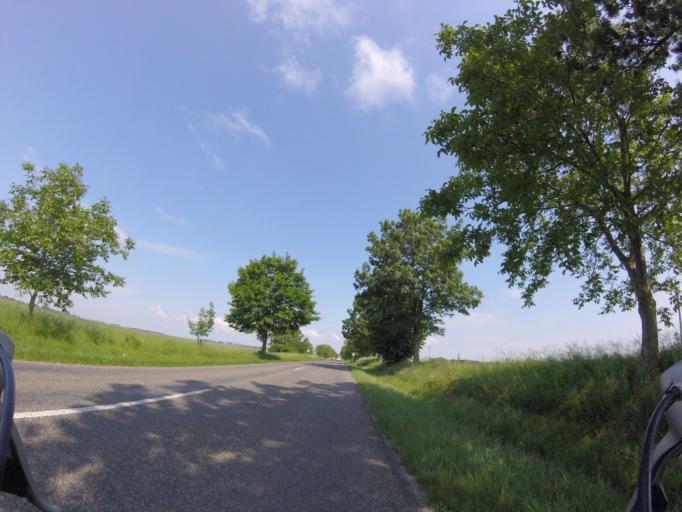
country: HU
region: Baranya
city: Kozarmisleny
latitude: 45.9834
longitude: 18.3336
